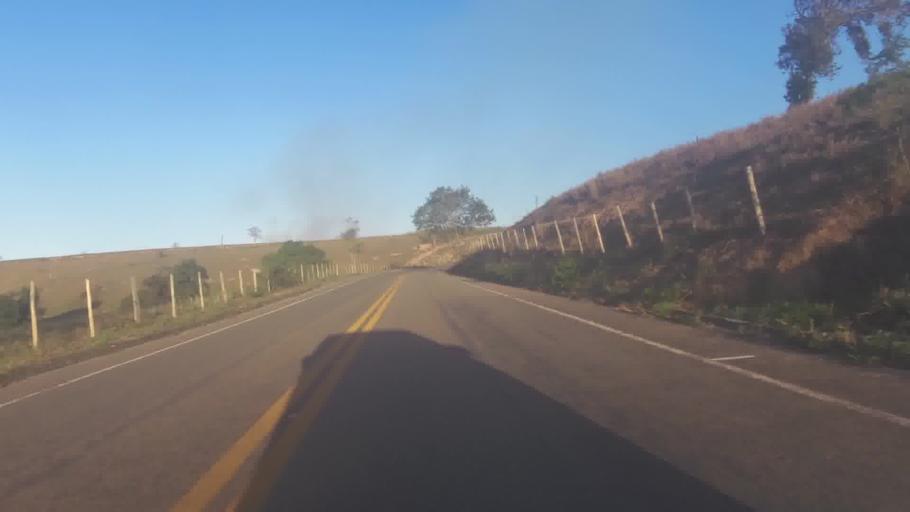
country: BR
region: Espirito Santo
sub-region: Marataizes
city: Marataizes
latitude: -21.1655
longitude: -40.9908
